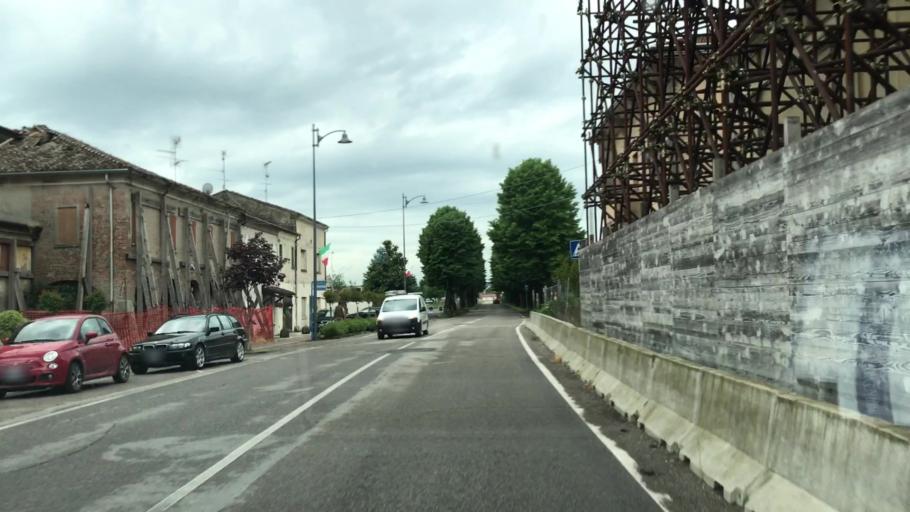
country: IT
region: Lombardy
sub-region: Provincia di Mantova
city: San Giovanni del Dosso
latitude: 44.9654
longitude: 11.0795
